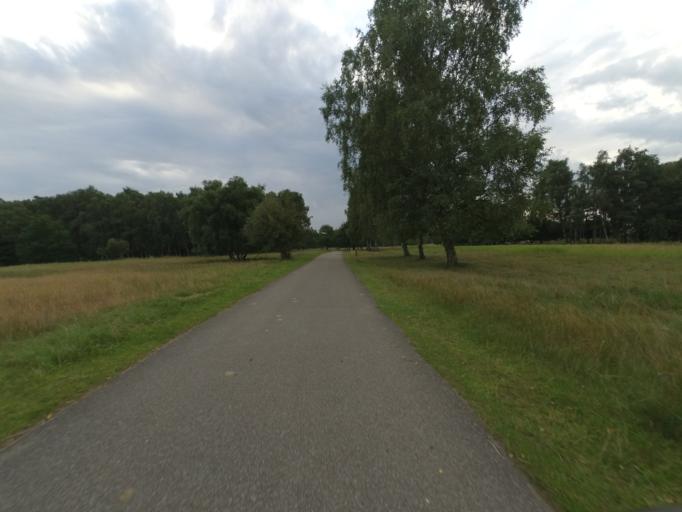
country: DE
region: Schleswig-Holstein
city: Oststeinbek
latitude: 53.5116
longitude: 10.1433
